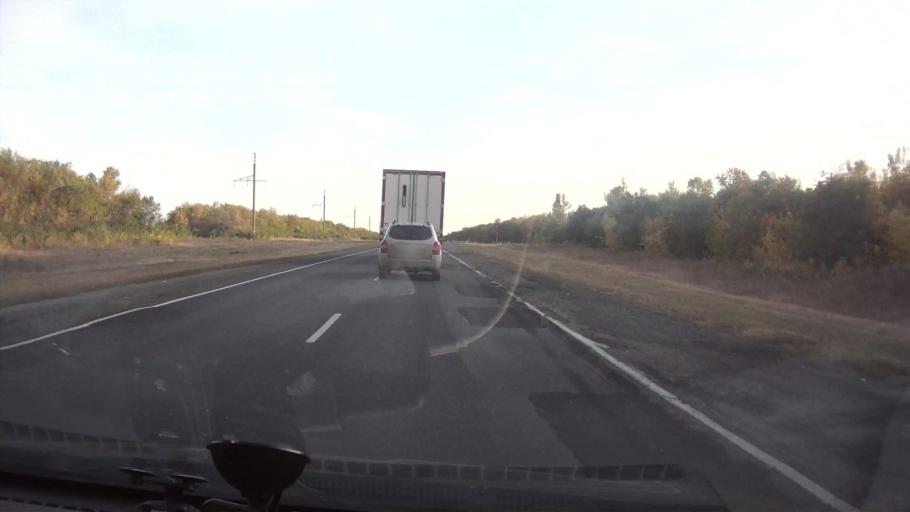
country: RU
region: Saratov
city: Krasnoarmeysk
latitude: 51.1295
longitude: 45.6505
